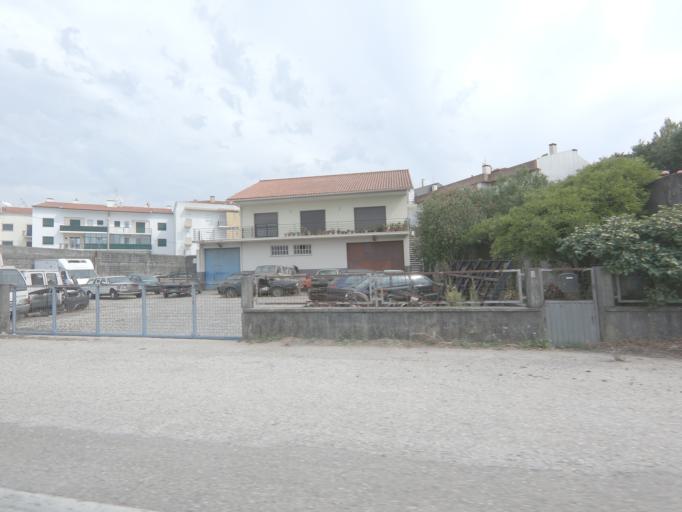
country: PT
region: Leiria
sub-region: Pombal
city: Pombal
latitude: 39.9026
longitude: -8.6355
